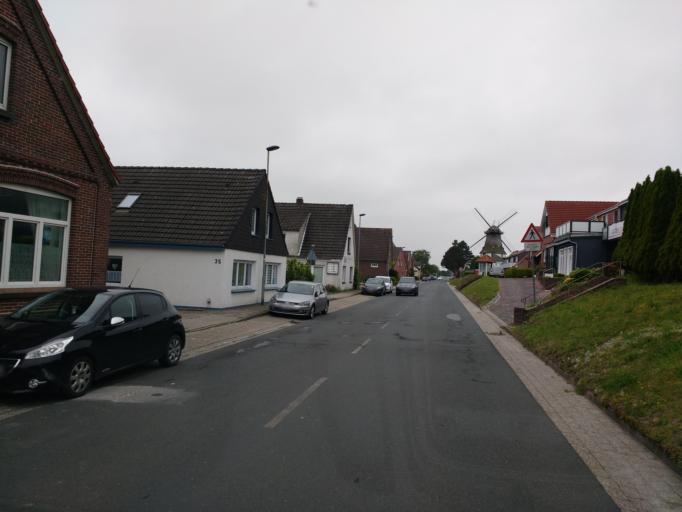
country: DE
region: Lower Saxony
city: Werdum
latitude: 53.6919
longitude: 7.7969
